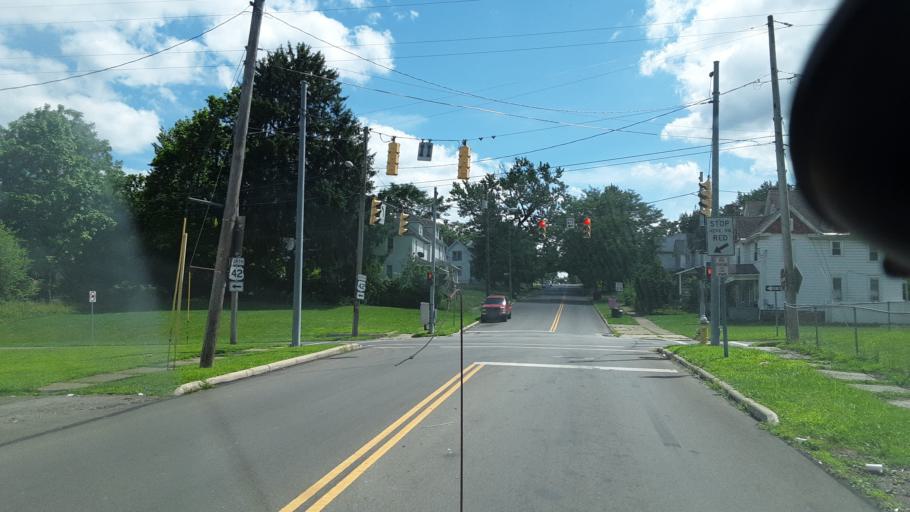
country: US
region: Ohio
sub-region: Richland County
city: Mansfield
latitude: 40.7562
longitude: -82.5098
